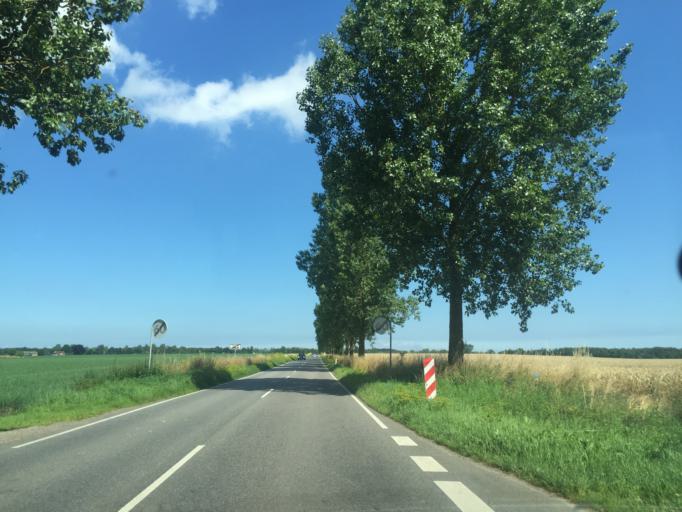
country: DK
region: South Denmark
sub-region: Nordfyns Kommune
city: Otterup
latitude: 55.5472
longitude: 10.3917
